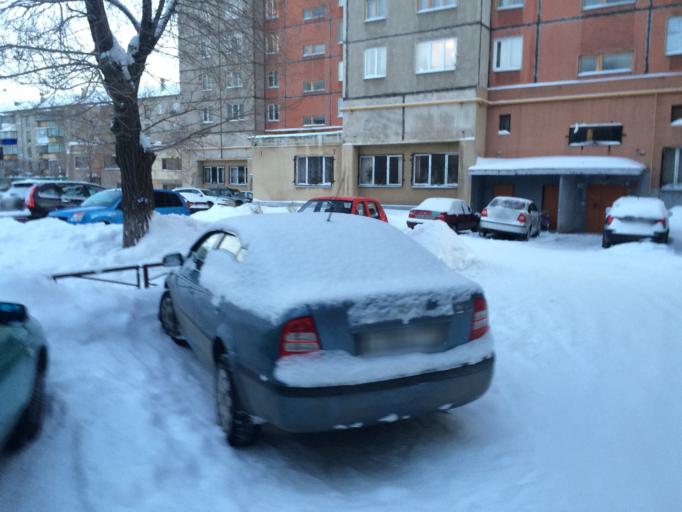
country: RU
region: Chelyabinsk
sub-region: Gorod Magnitogorsk
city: Magnitogorsk
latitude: 53.4055
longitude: 58.9722
